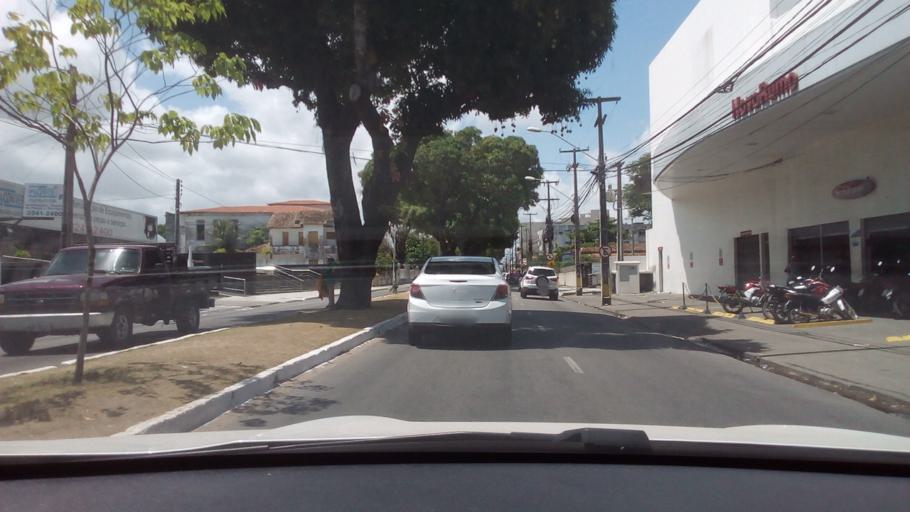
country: BR
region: Paraiba
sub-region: Joao Pessoa
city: Joao Pessoa
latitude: -7.1261
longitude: -34.8791
